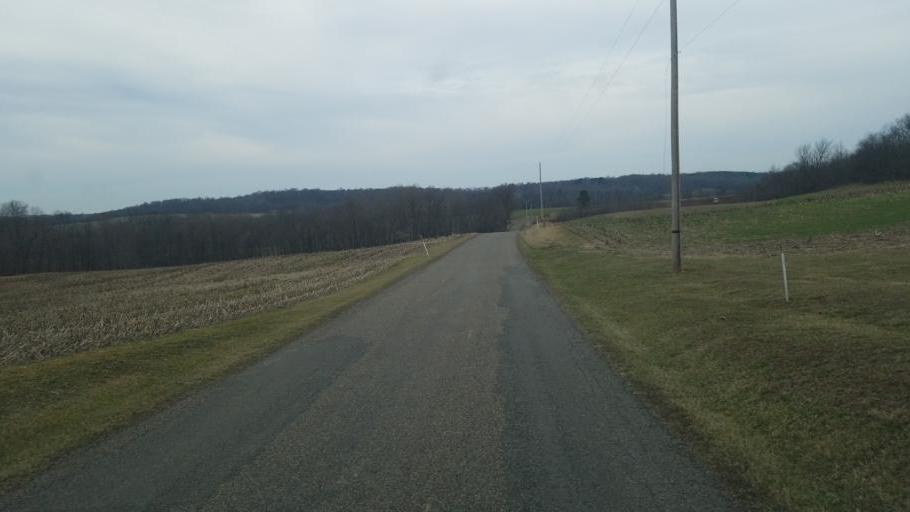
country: US
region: Ohio
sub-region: Ashland County
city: Loudonville
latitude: 40.7066
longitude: -82.3094
